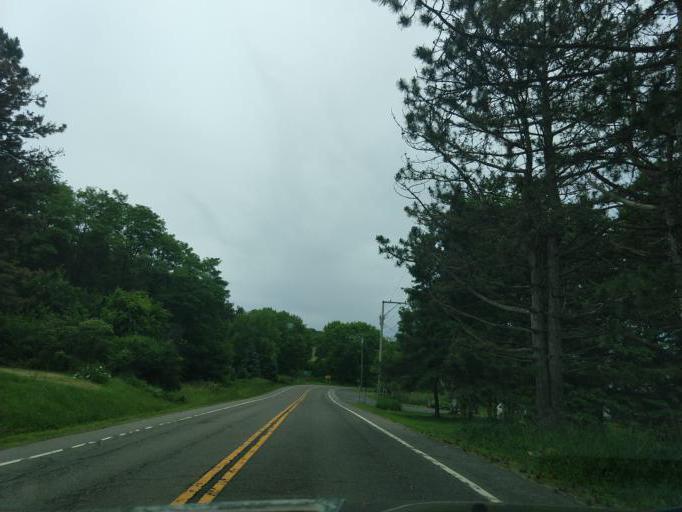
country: US
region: New York
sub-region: Tompkins County
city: Dryden
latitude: 42.4913
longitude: -76.2745
